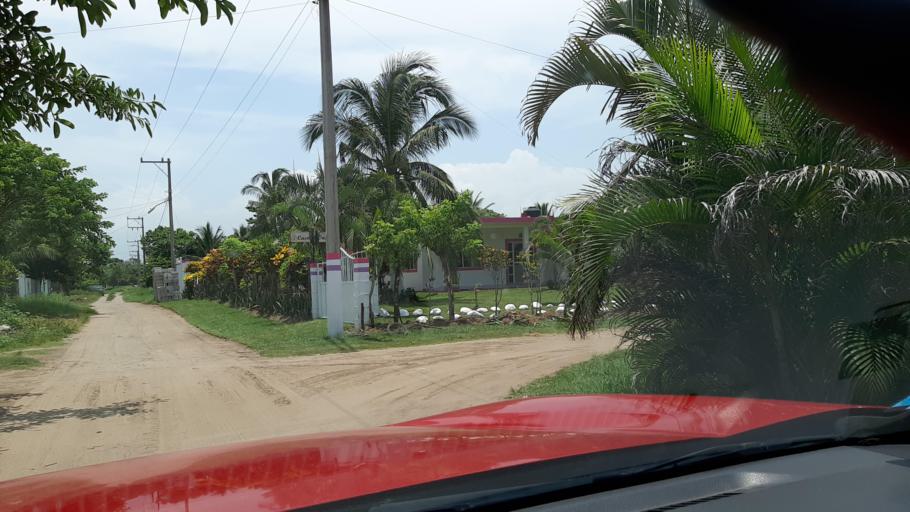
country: MX
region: Veracruz
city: San Rafael
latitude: 20.2929
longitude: -96.8418
